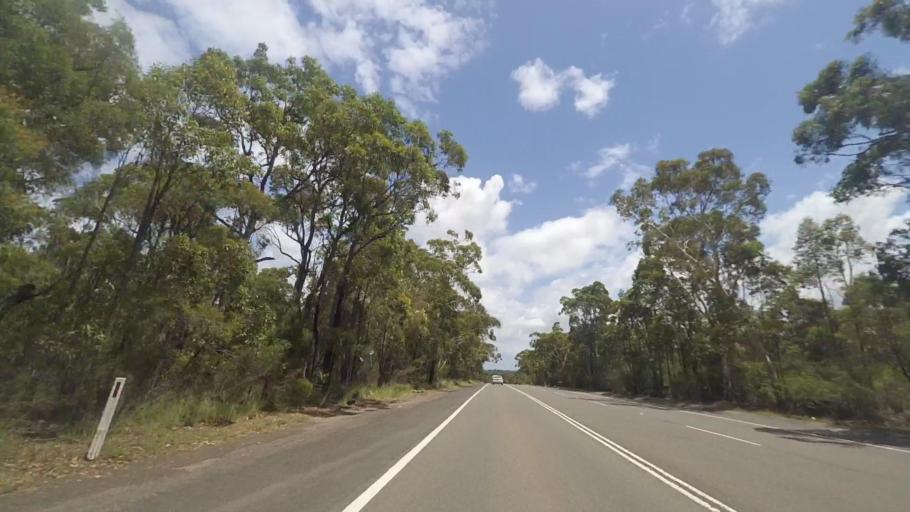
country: AU
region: New South Wales
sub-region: Liverpool
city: East Hills
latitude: -33.9697
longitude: 150.9769
